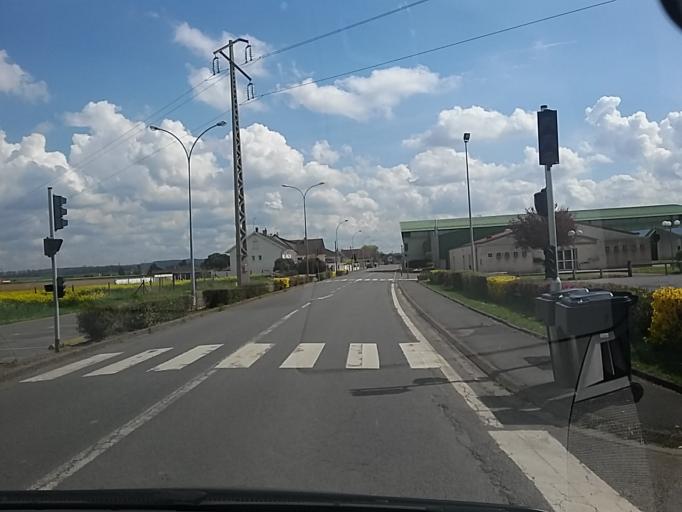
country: FR
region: Picardie
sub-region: Departement de l'Oise
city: Chevrieres
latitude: 49.3464
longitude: 2.6663
